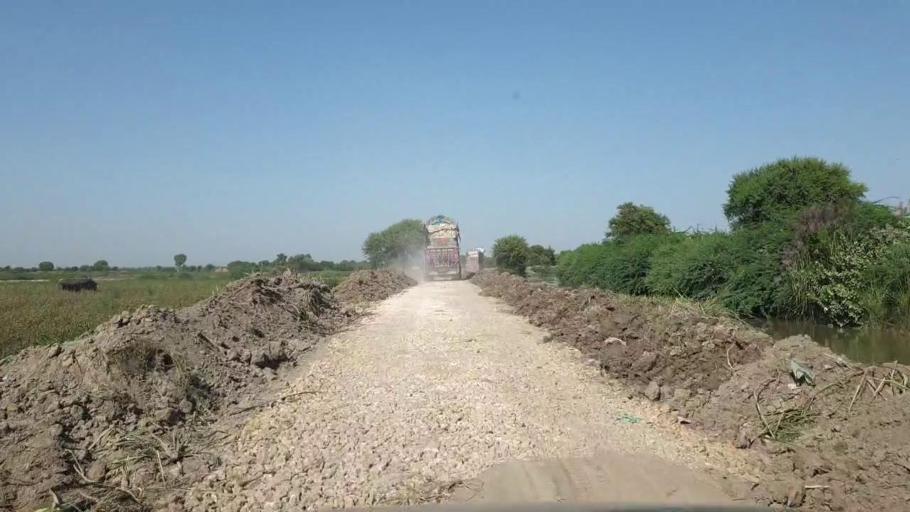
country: PK
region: Sindh
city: Kadhan
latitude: 24.5292
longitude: 69.0005
